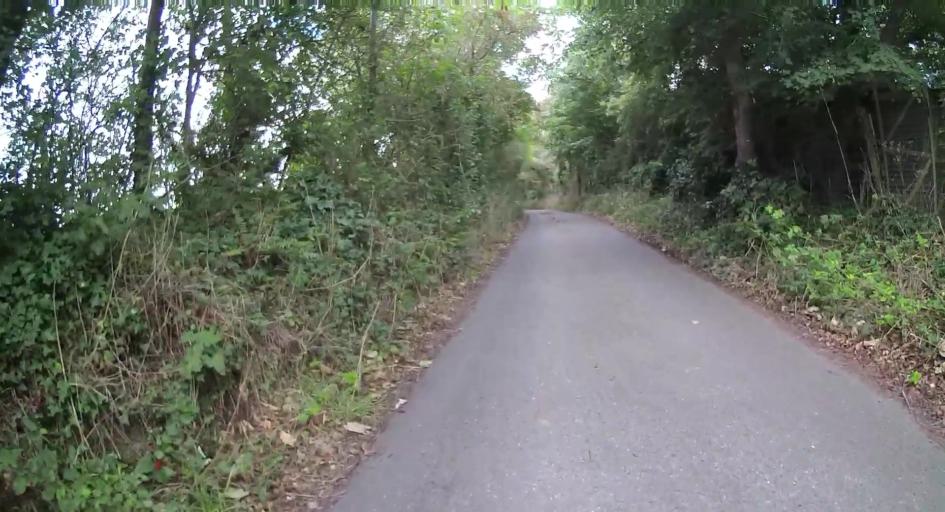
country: GB
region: England
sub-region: Isle of Wight
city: Niton
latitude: 50.6296
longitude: -1.2685
